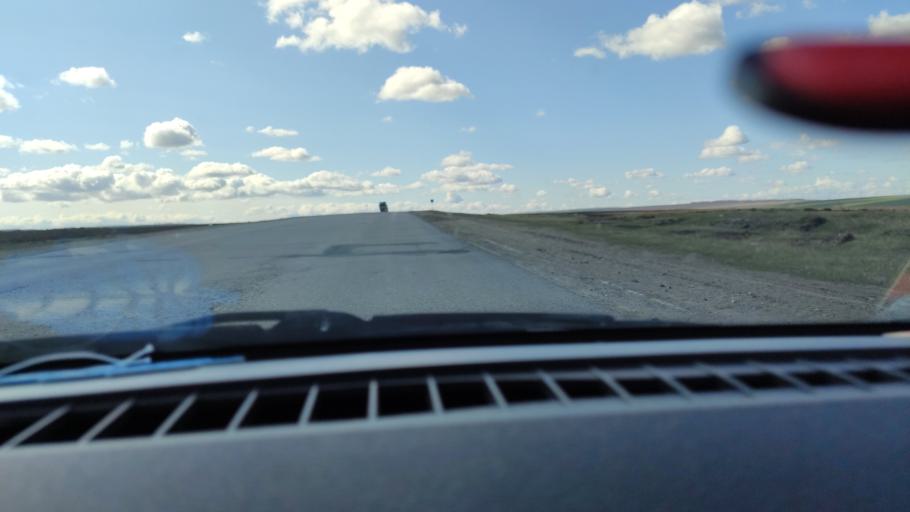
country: RU
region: Samara
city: Varlamovo
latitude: 53.0577
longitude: 48.3494
